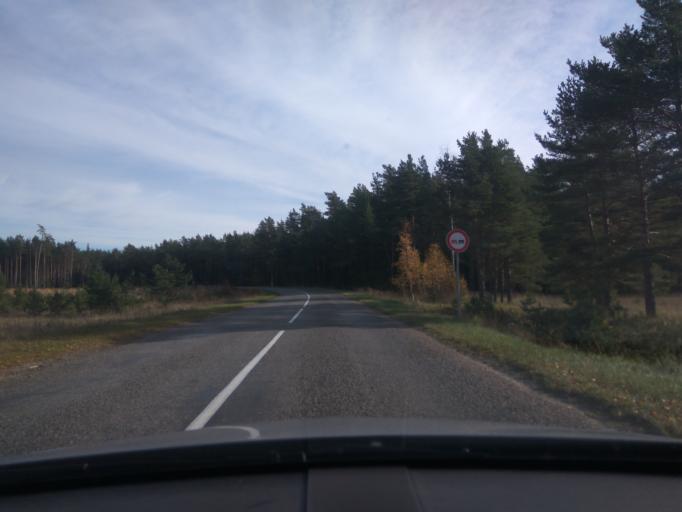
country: LV
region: Alsunga
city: Alsunga
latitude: 57.0108
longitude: 21.3985
